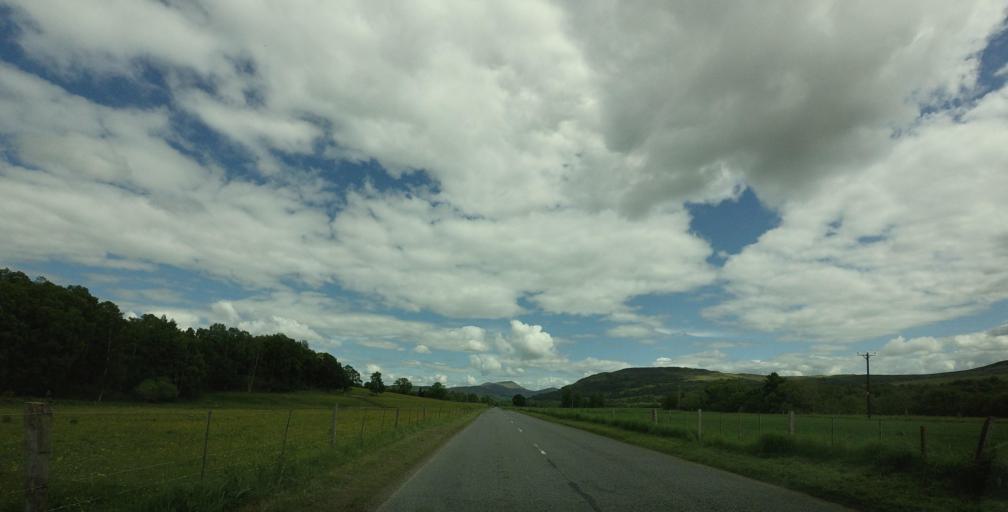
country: GB
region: Scotland
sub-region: Perth and Kinross
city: Aberfeldy
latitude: 56.7708
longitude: -3.9190
